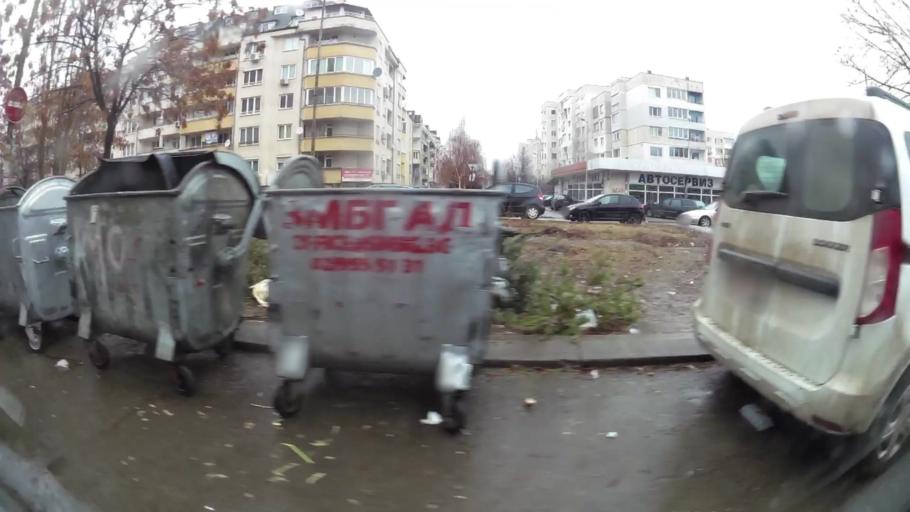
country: BG
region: Sofia-Capital
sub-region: Stolichna Obshtina
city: Sofia
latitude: 42.6353
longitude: 23.3763
